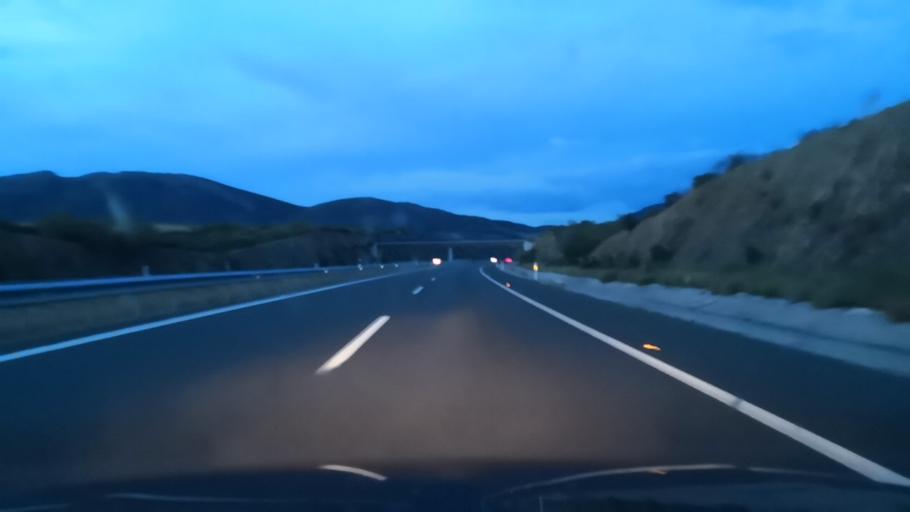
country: ES
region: Extremadura
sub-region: Provincia de Caceres
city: Canaveral
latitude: 39.7657
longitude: -6.3977
